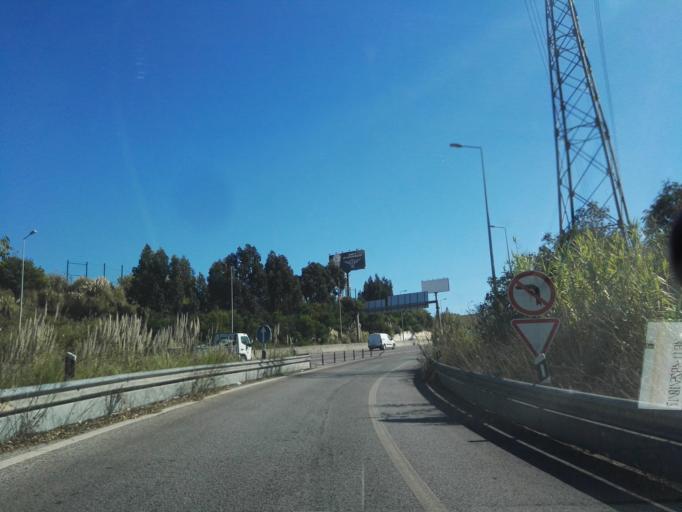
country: PT
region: Lisbon
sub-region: Sintra
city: Rio de Mouro
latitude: 38.7756
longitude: -9.3220
